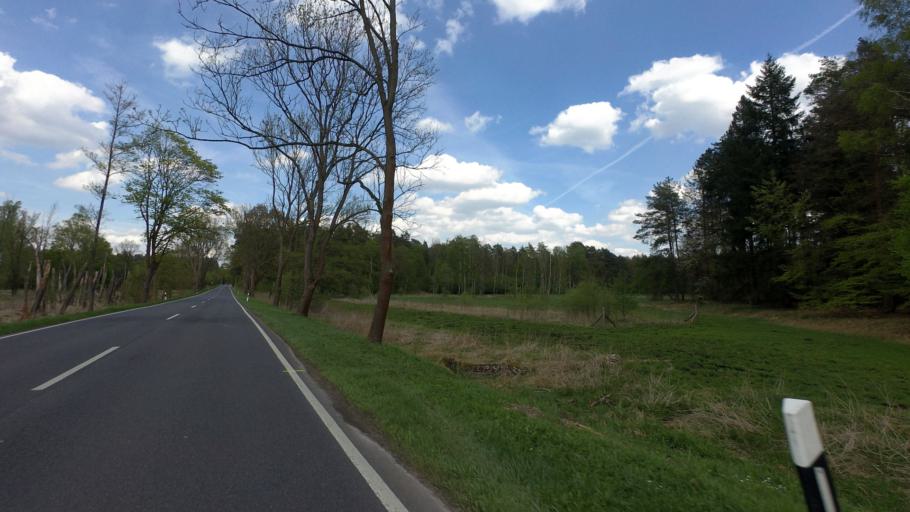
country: DE
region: Brandenburg
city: Friedrichswalde
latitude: 52.9789
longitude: 13.5816
